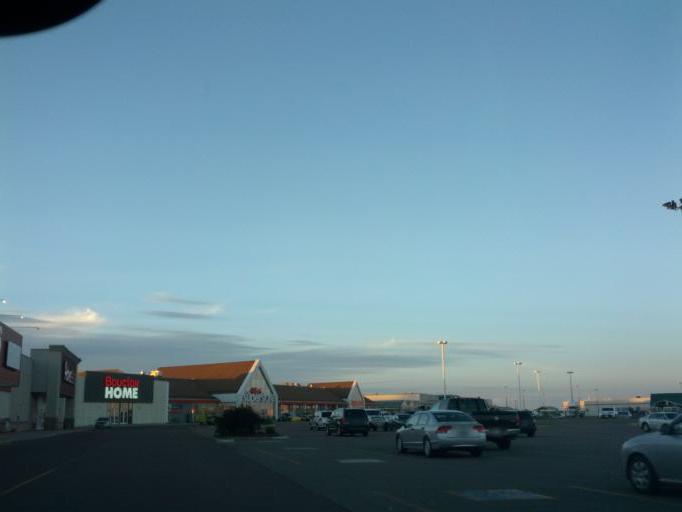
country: CA
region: New Brunswick
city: Moncton
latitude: 46.1168
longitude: -64.8336
